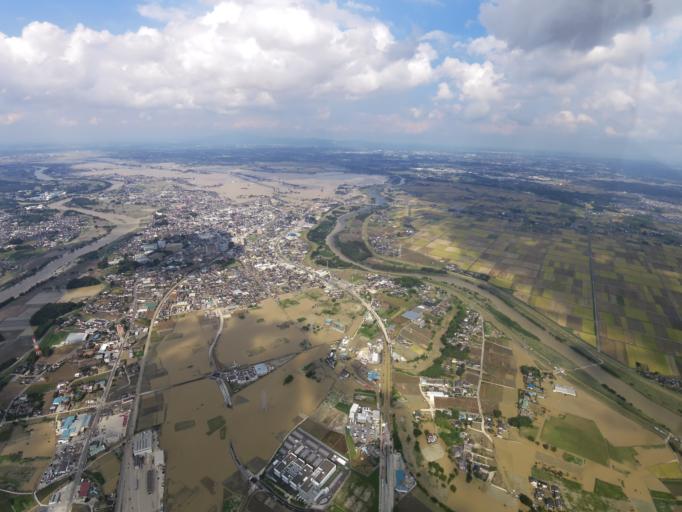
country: JP
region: Ibaraki
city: Mitsukaido
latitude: 36.0011
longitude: 139.9814
